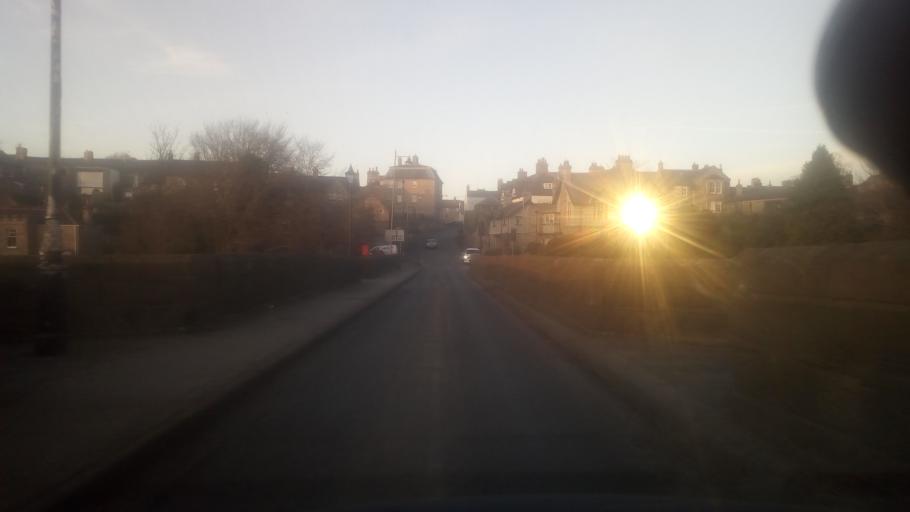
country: GB
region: England
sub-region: Northumberland
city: Corbridge
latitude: 54.9723
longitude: -2.0188
